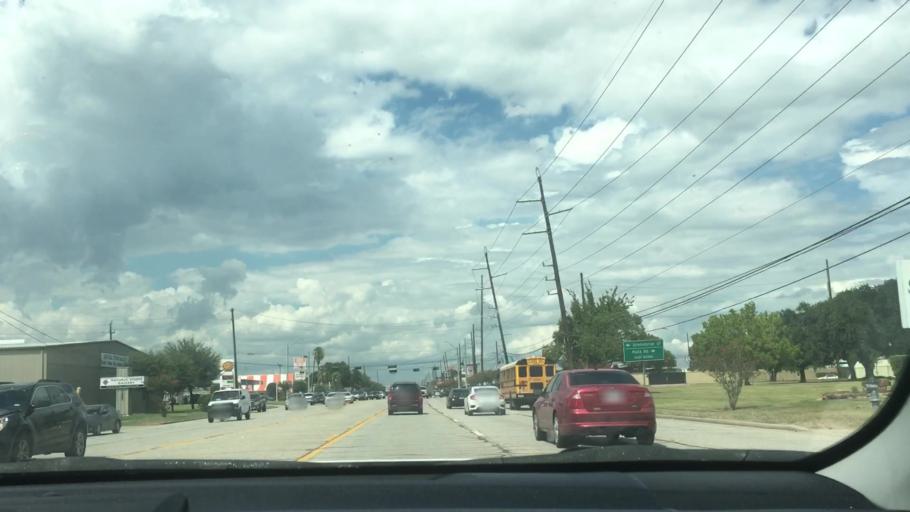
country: US
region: Texas
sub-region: Fort Bend County
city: Stafford
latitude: 29.6310
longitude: -95.5649
